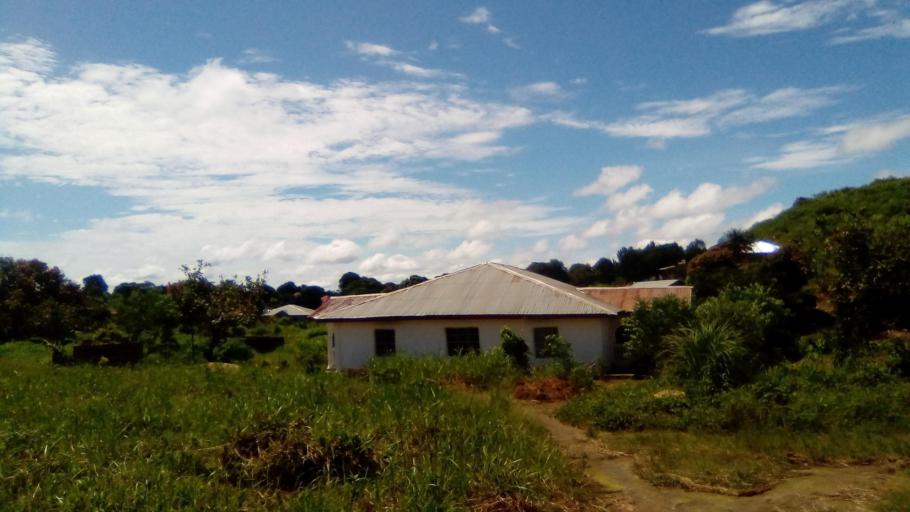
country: SL
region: Eastern Province
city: Koidu
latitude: 8.6359
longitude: -10.9949
